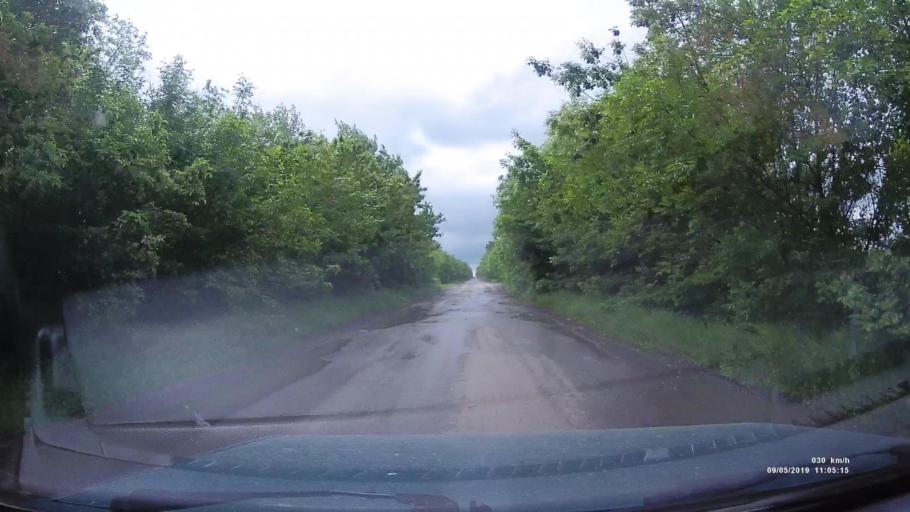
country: RU
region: Krasnodarskiy
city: Kanelovskaya
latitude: 46.8109
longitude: 39.2099
